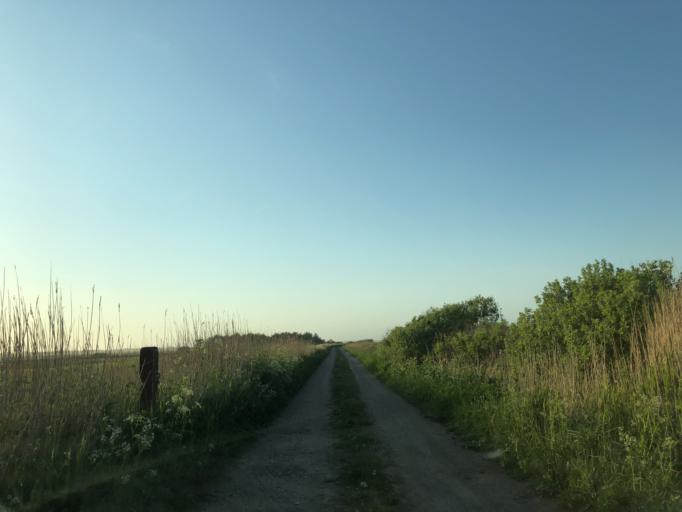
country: DK
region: Central Jutland
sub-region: Ringkobing-Skjern Kommune
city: Ringkobing
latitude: 56.2038
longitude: 8.1608
